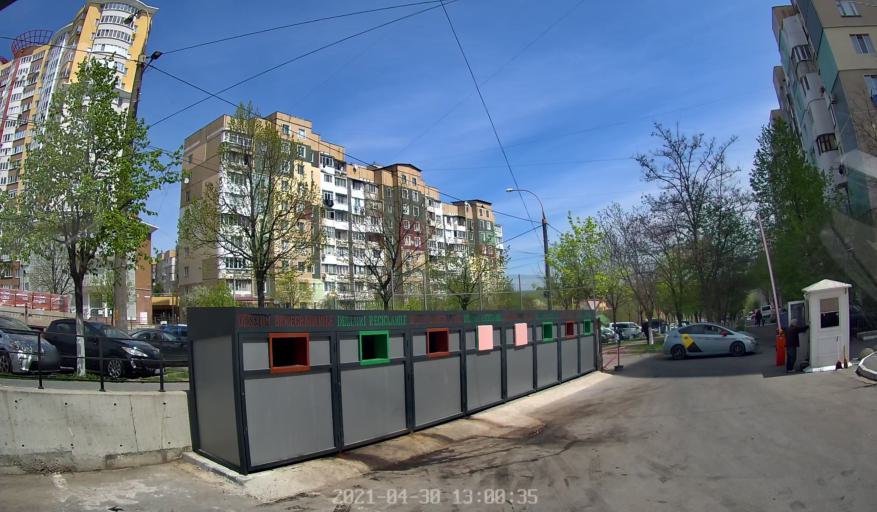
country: NG
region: Niger
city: Lemu
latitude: 9.4113
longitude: 5.7786
